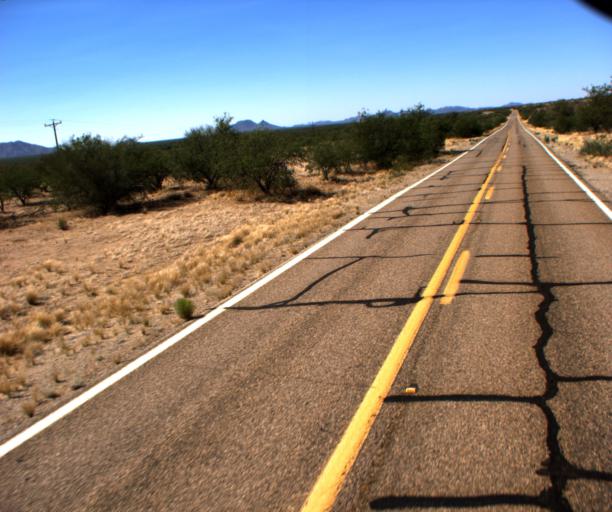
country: US
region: Arizona
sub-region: Pima County
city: Three Points
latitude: 31.8970
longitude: -111.3921
